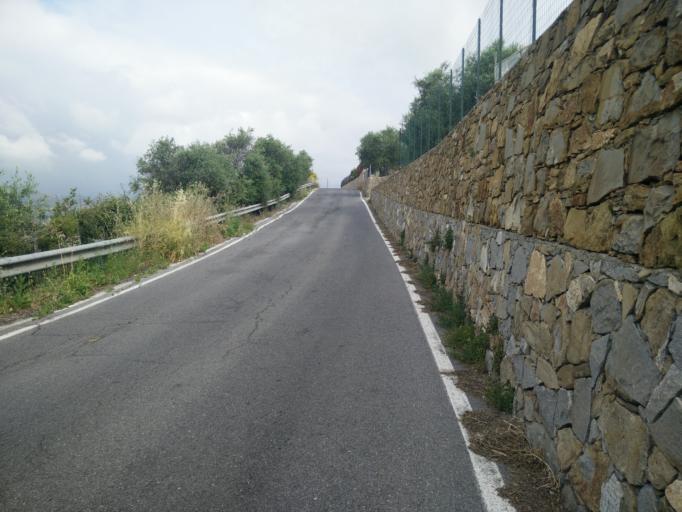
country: IT
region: Liguria
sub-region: Provincia di Imperia
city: Imperia
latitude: 43.8765
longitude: 7.9985
